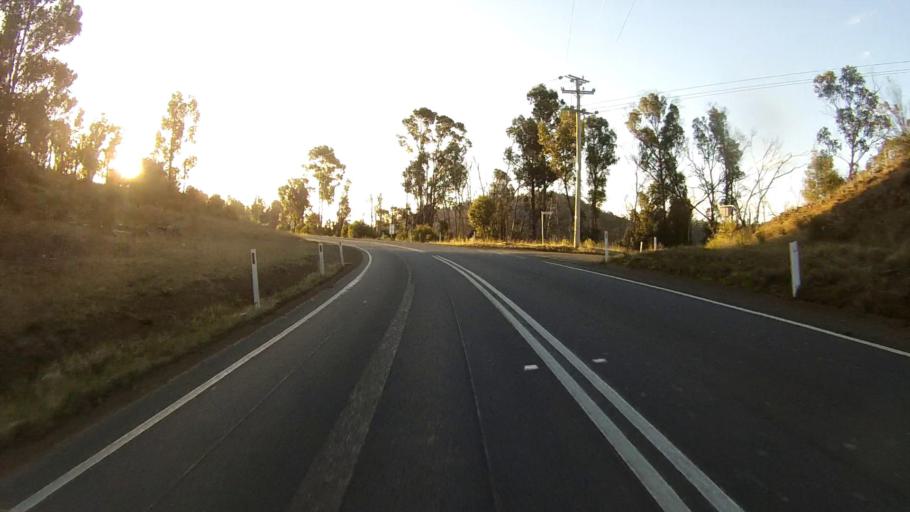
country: AU
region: Tasmania
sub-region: Sorell
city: Sorell
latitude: -42.8528
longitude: 147.8227
